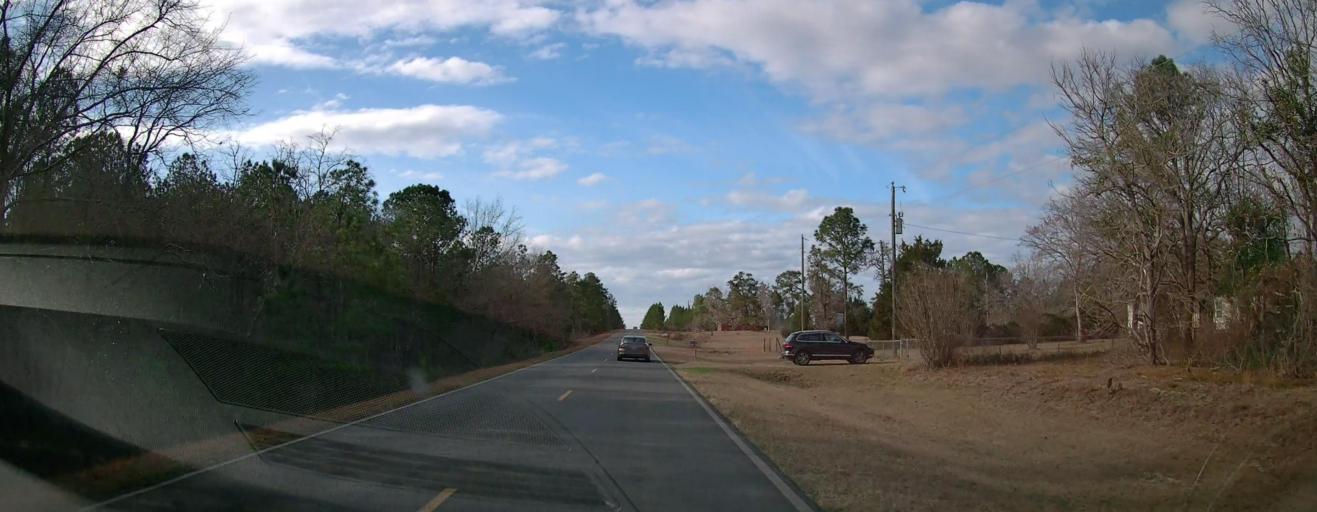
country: US
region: Georgia
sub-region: Talbot County
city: Talbotton
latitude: 32.5089
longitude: -84.5894
